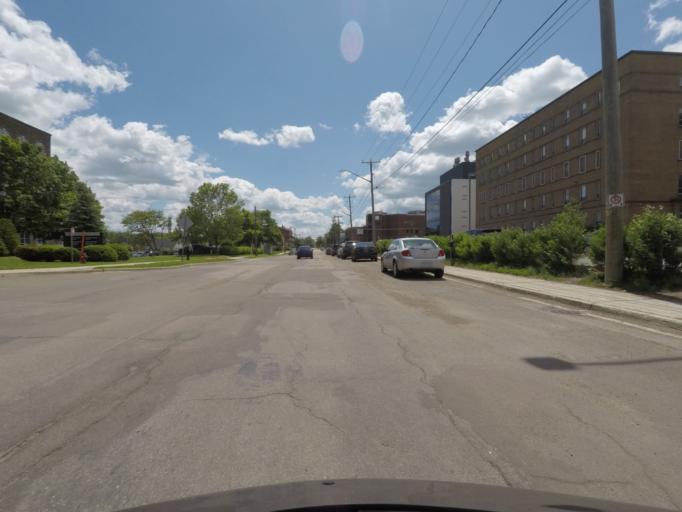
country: CA
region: New Brunswick
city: Moncton
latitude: 46.0980
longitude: -64.7860
